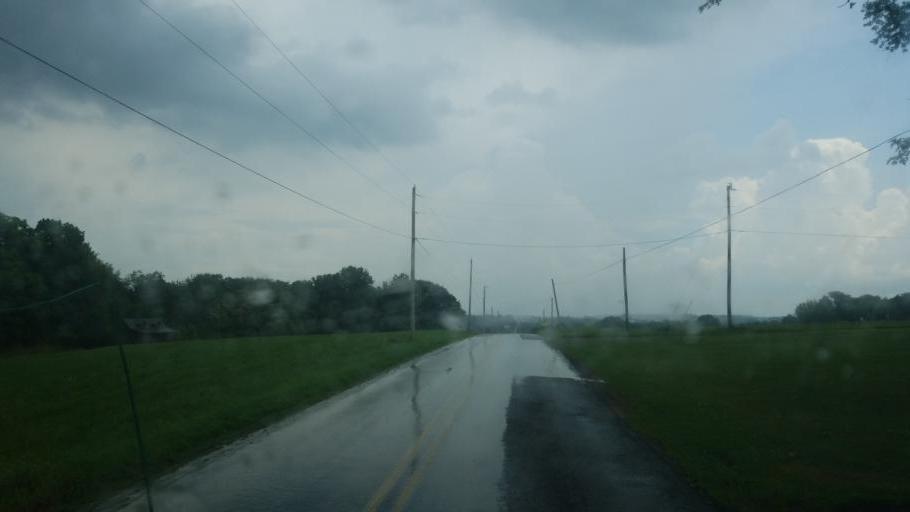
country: US
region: Ohio
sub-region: Wayne County
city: Smithville
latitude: 40.9018
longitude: -81.8335
